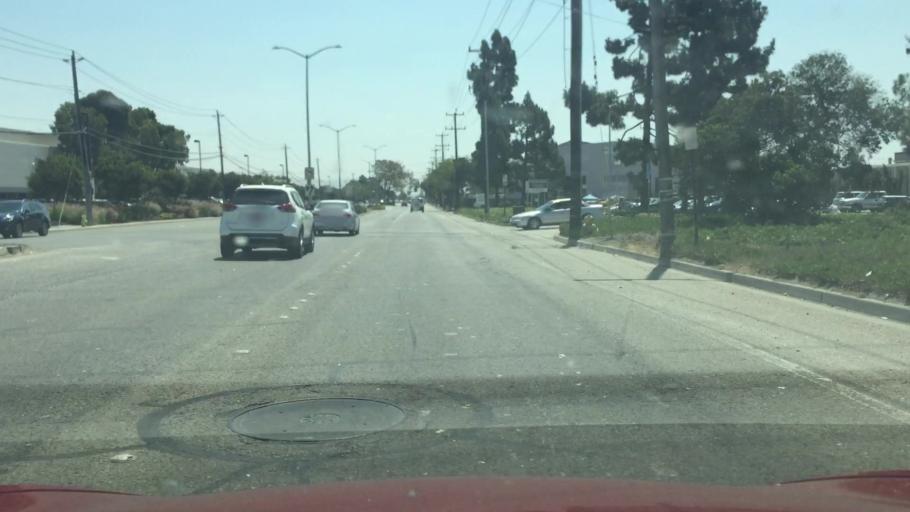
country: US
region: California
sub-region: Alameda County
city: Fremont
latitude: 37.5092
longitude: -121.9886
